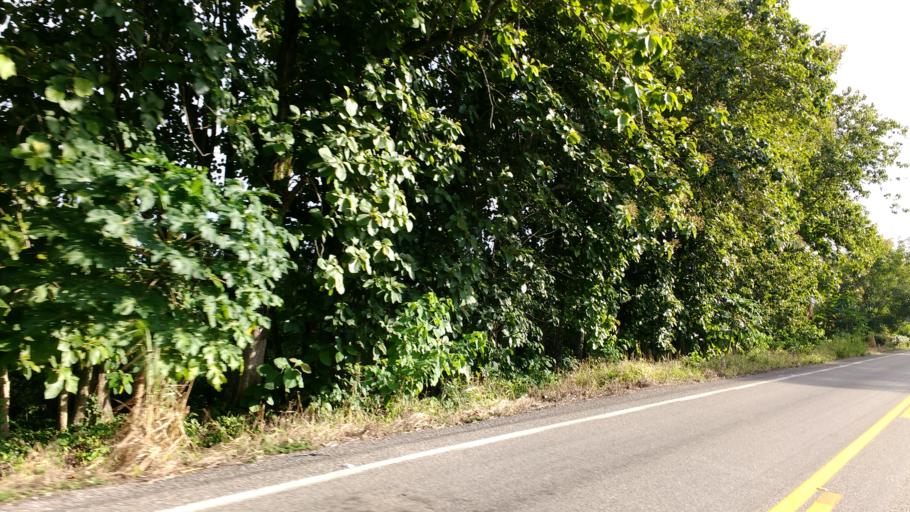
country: MX
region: Tabasco
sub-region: Teapa
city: Eureka y Belen
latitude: 17.6700
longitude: -92.9502
